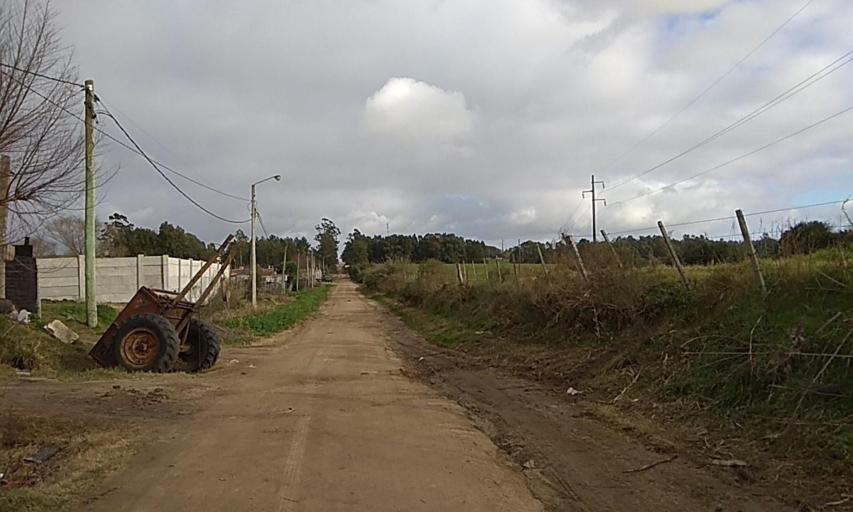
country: UY
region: Florida
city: Florida
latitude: -34.0768
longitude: -56.2255
